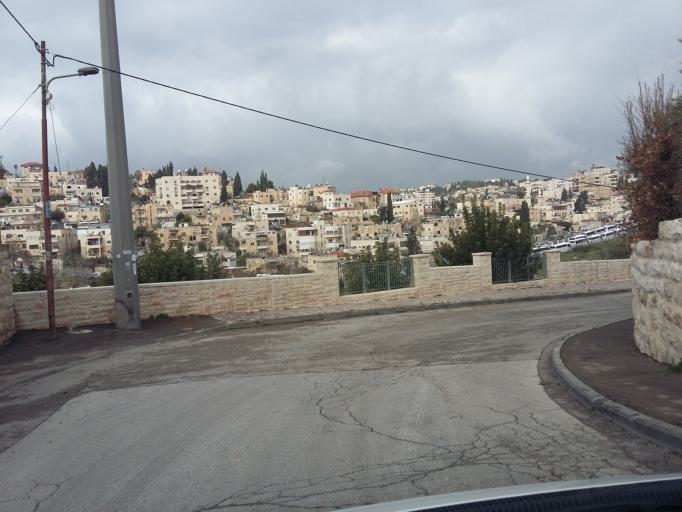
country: PS
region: West Bank
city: East Jerusalem
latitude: 31.7850
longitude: 35.2405
